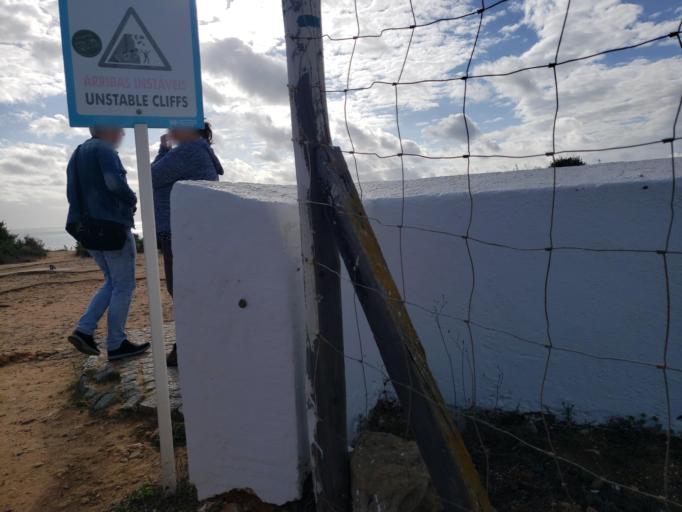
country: PT
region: Faro
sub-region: Lagos
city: Lagos
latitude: 37.0802
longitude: -8.6692
